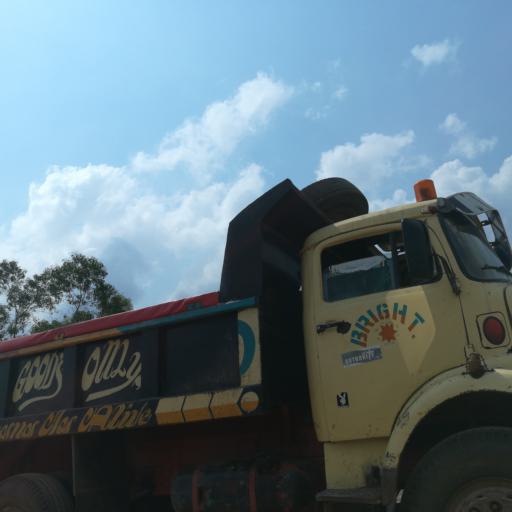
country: NG
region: Rivers
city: Okrika
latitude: 4.8062
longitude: 7.1020
